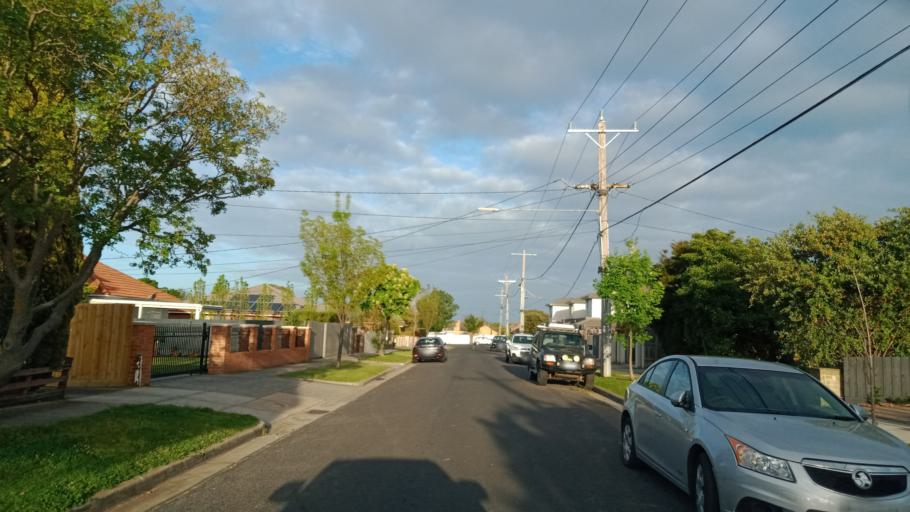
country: AU
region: Victoria
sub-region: Bayside
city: Moorabbin
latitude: -37.9337
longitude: 145.0498
